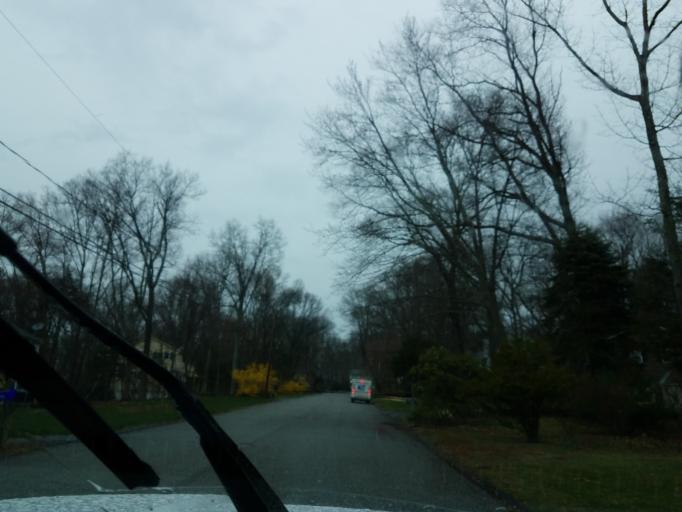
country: US
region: Connecticut
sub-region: Tolland County
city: Tolland
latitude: 41.8654
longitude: -72.4085
